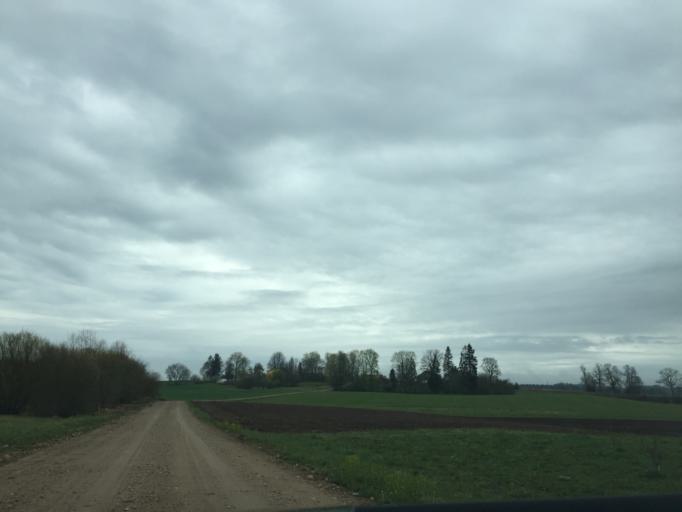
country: LV
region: Malpils
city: Malpils
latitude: 57.0250
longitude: 24.8466
